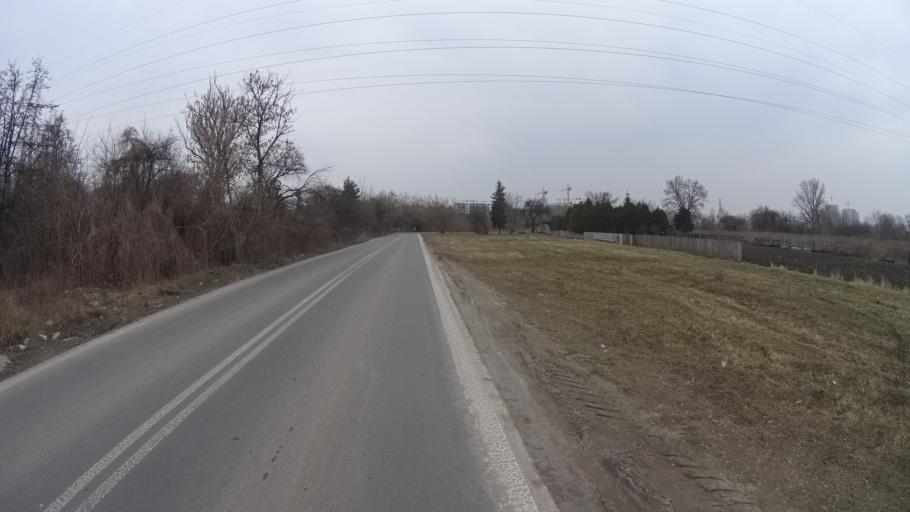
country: PL
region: Masovian Voivodeship
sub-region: Warszawa
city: Wlochy
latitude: 52.2185
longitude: 20.9435
